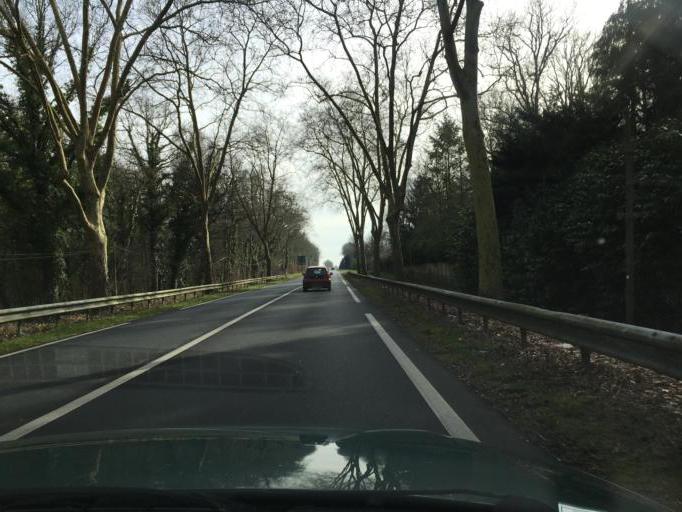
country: FR
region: Centre
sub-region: Departement du Loiret
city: Saint-Cyr-en-Val
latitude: 47.8116
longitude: 1.9288
